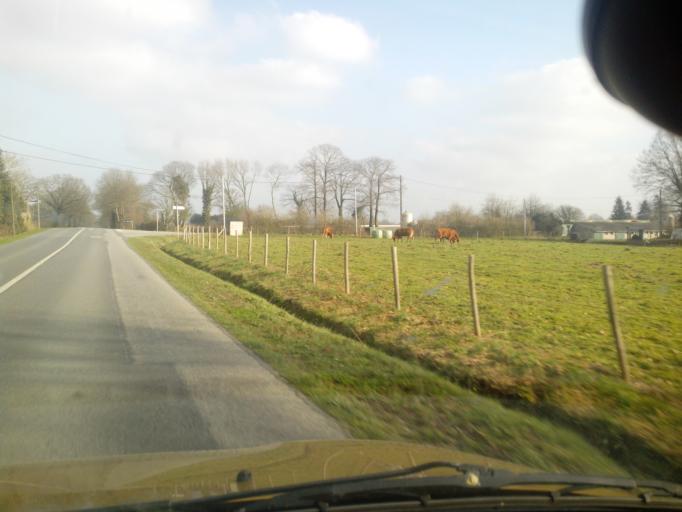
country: FR
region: Brittany
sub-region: Departement du Morbihan
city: Questembert
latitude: 47.6925
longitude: -2.4870
